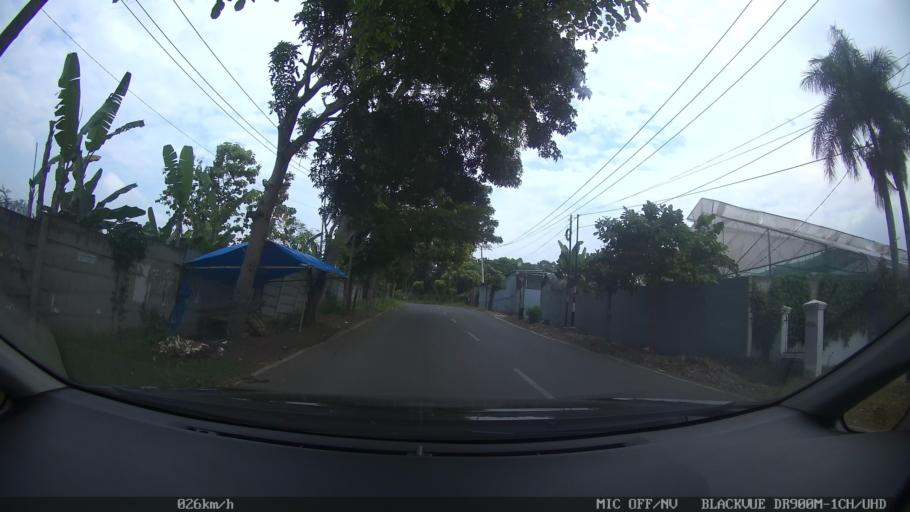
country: ID
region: Lampung
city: Bandarlampung
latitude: -5.4349
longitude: 105.2477
